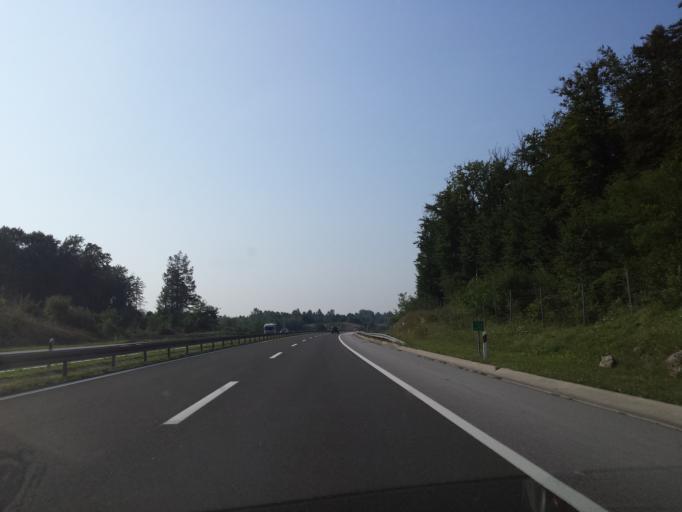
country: HR
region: Karlovacka
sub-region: Grad Ogulin
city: Ogulin
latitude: 45.3592
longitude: 15.2759
